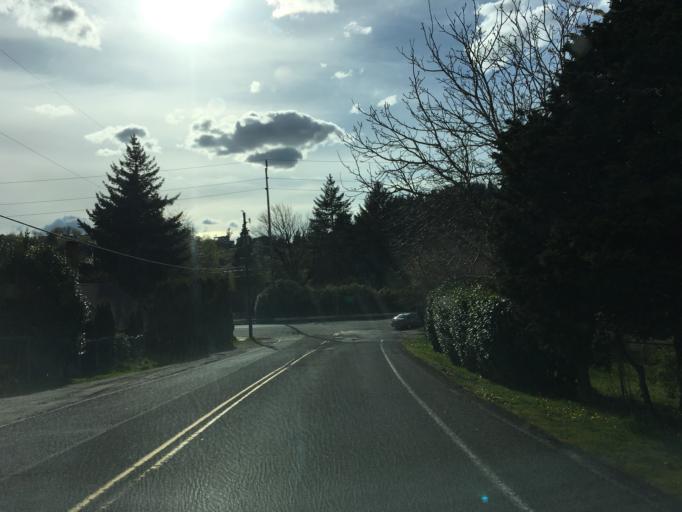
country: US
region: Oregon
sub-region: Multnomah County
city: Lents
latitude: 45.5441
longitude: -122.5570
